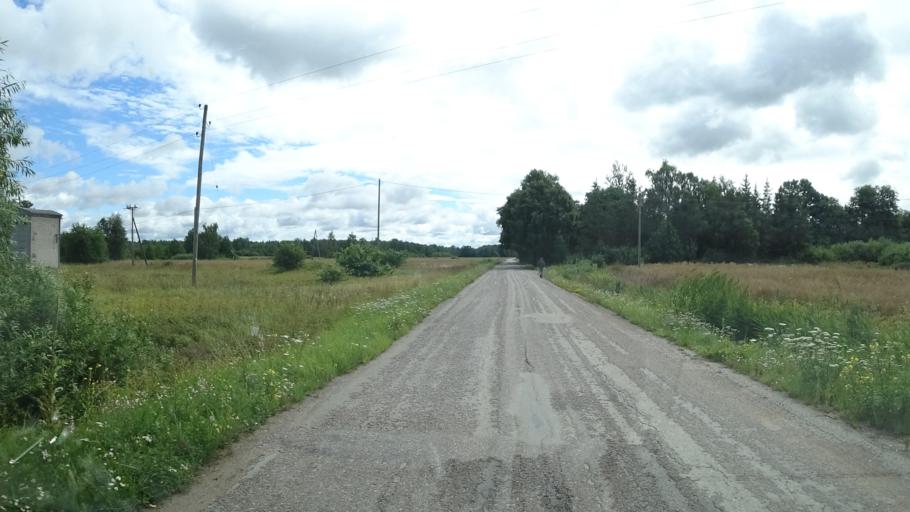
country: LV
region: Liepaja
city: Vec-Liepaja
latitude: 56.6610
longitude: 21.0779
